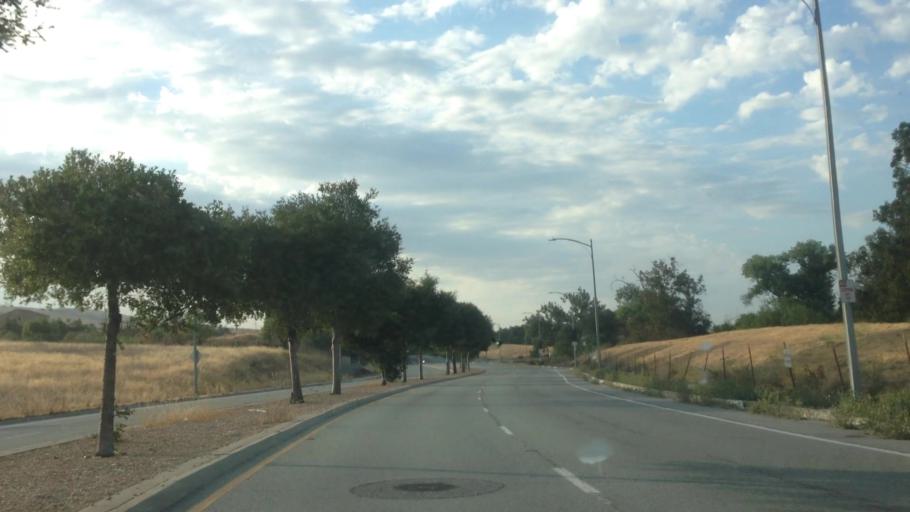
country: US
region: California
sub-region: Santa Clara County
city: Seven Trees
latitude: 37.2519
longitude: -121.7730
